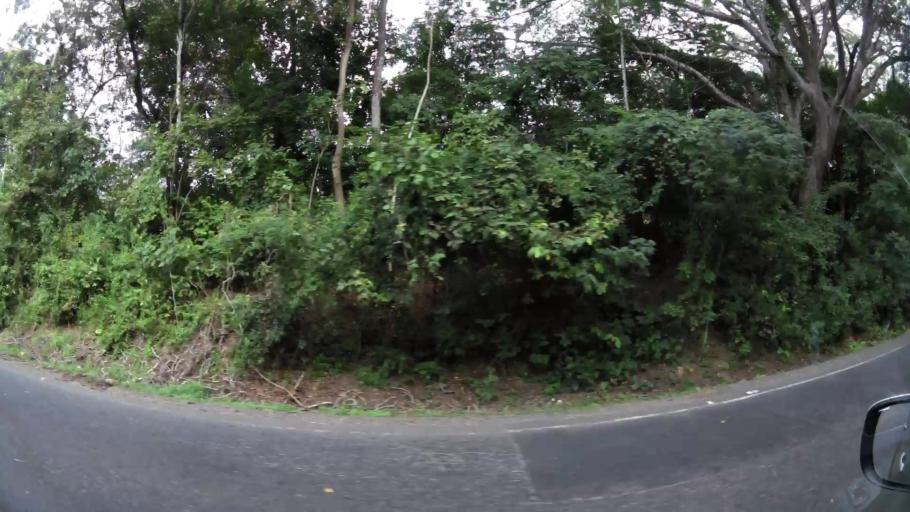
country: CR
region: Guanacaste
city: Juntas
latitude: 10.1544
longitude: -84.9142
